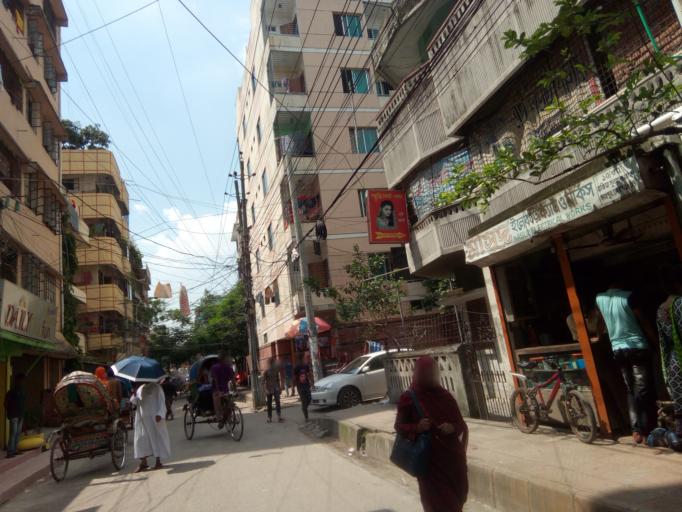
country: BD
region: Dhaka
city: Azimpur
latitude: 23.7624
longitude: 90.3616
